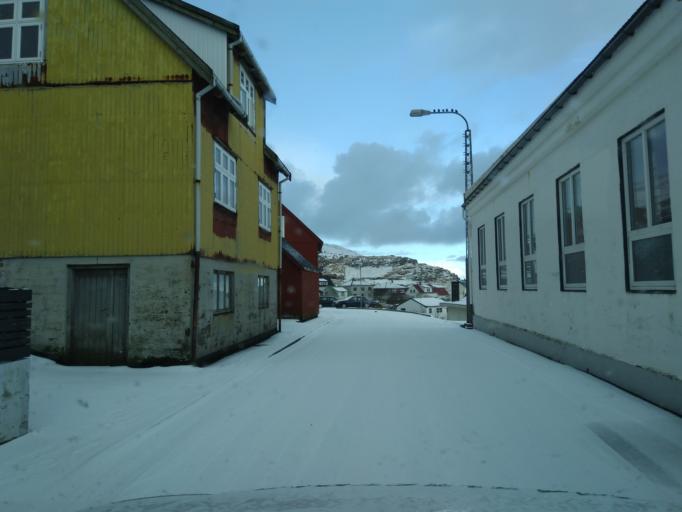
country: FO
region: Eysturoy
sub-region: Eidi
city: Eidi
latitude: 62.3001
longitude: -7.0923
